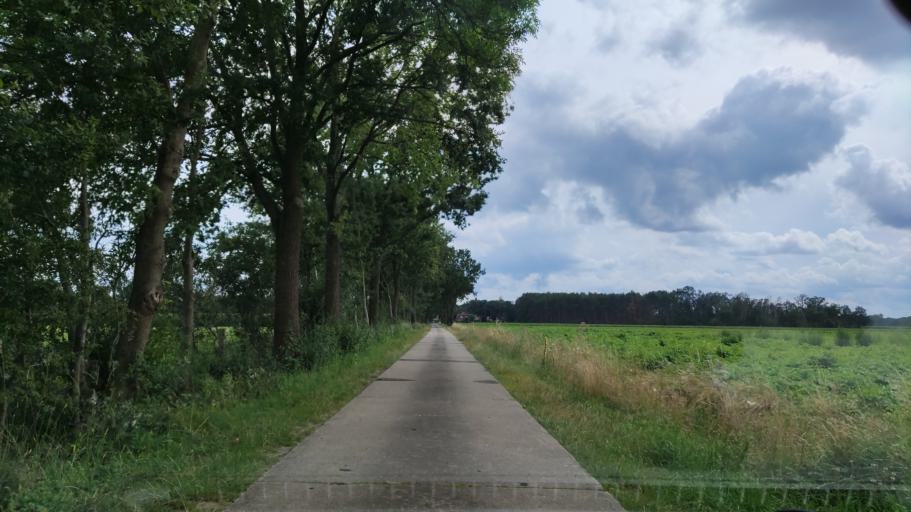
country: DE
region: Lower Saxony
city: Damnatz
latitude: 53.1016
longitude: 11.1445
